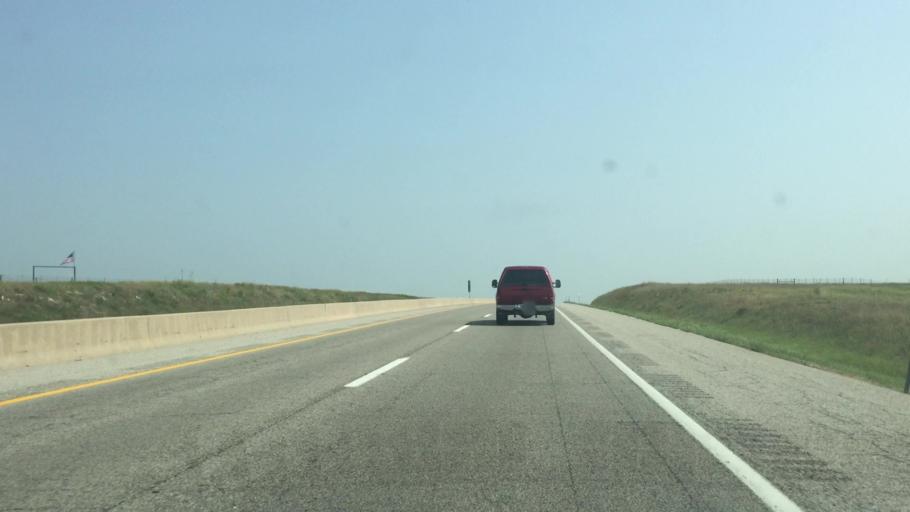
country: US
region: Kansas
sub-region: Lyon County
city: Emporia
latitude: 38.2993
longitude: -96.3506
